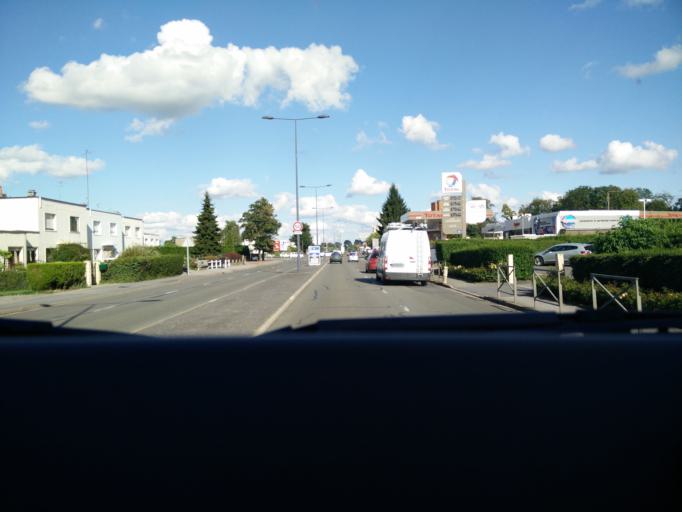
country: FR
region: Nord-Pas-de-Calais
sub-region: Departement du Nord
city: Maubeuge
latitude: 50.2824
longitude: 3.9689
